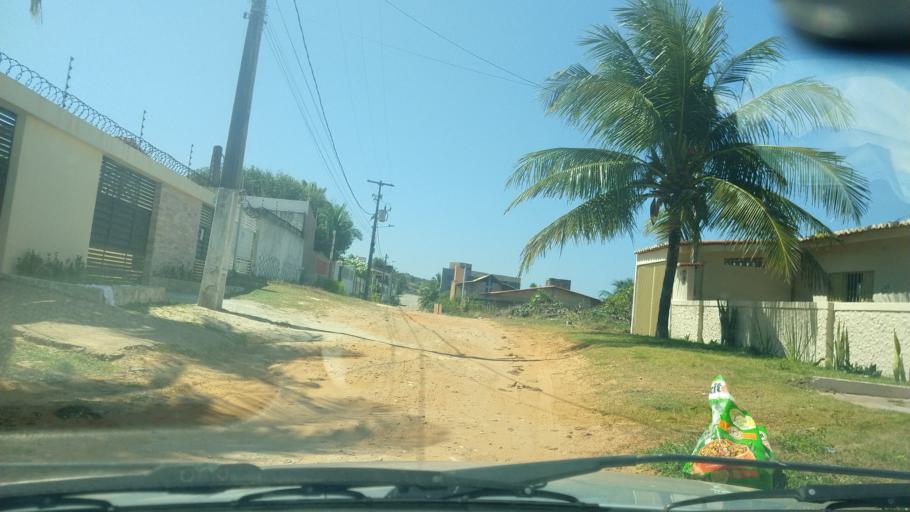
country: BR
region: Rio Grande do Norte
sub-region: Parnamirim
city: Parnamirim
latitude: -5.9527
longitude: -35.1529
